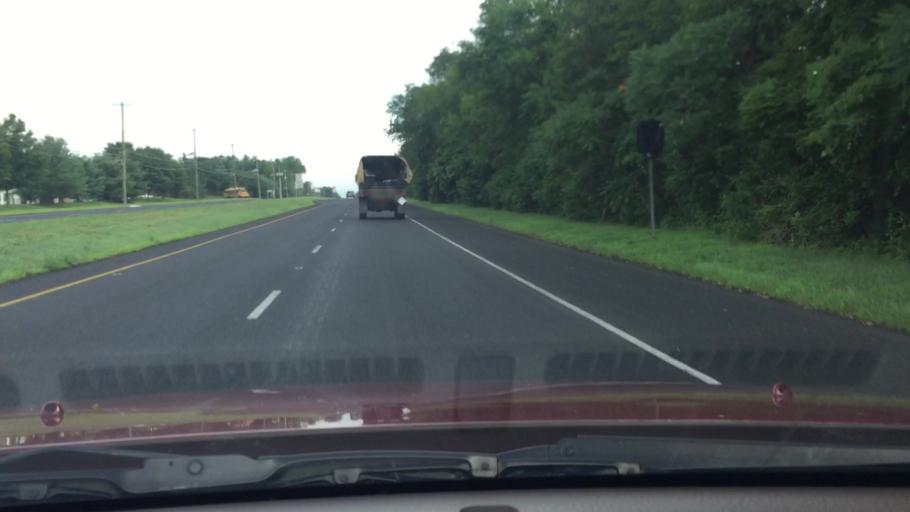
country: US
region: New Jersey
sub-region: Burlington County
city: Bordentown
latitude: 40.0918
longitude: -74.6794
